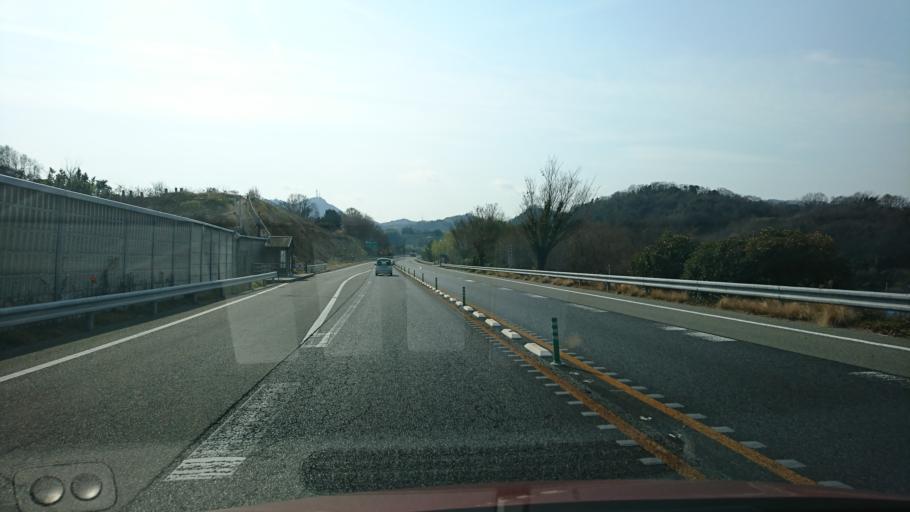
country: JP
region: Hiroshima
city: Onomichi
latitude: 34.3985
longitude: 133.2087
